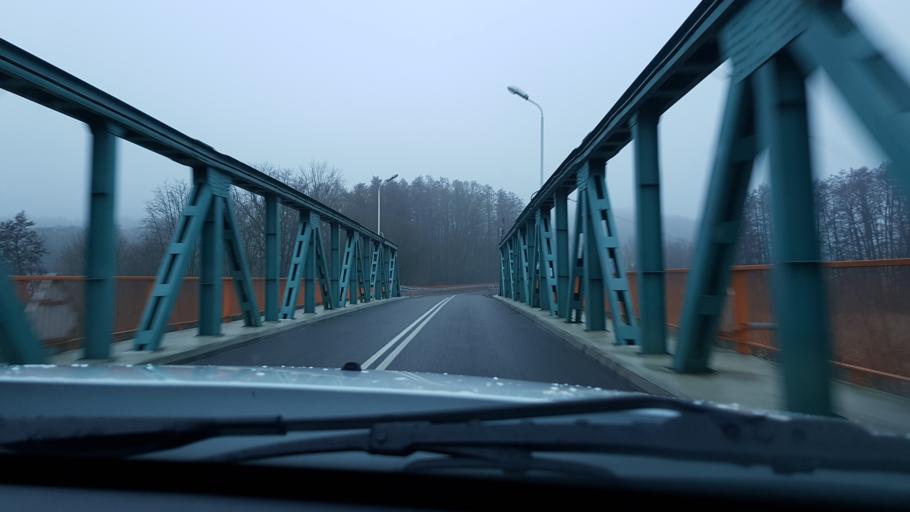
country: DE
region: Brandenburg
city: Mescherin
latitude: 53.2549
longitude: 14.4418
